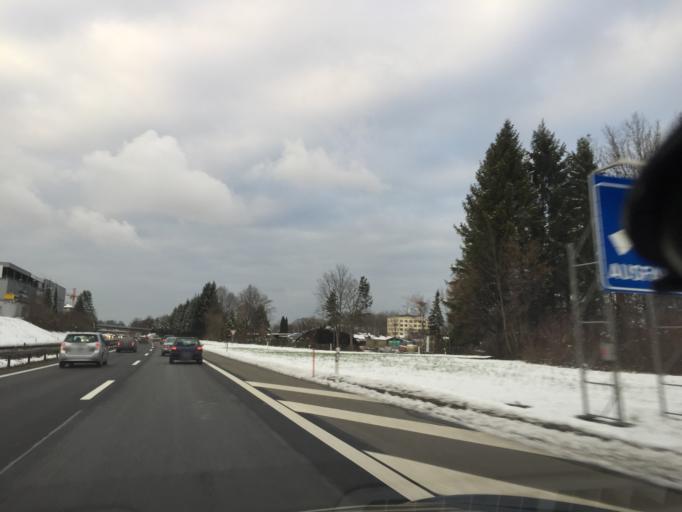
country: CH
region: Zurich
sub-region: Bezirk Horgen
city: Ruschlikon
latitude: 47.3018
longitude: 8.5477
